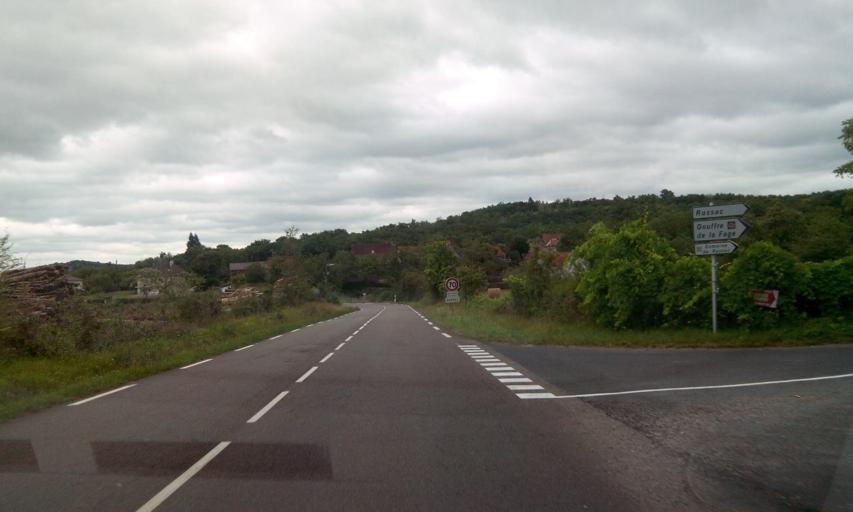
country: FR
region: Limousin
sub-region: Departement de la Correze
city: Cosnac
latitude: 45.0642
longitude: 1.5634
